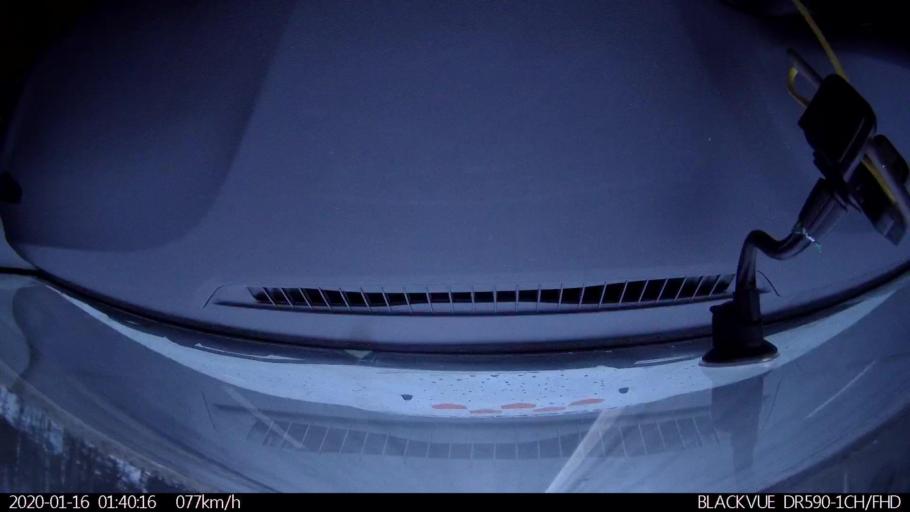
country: RU
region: Nizjnij Novgorod
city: Gorbatovka
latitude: 56.3281
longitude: 43.7814
